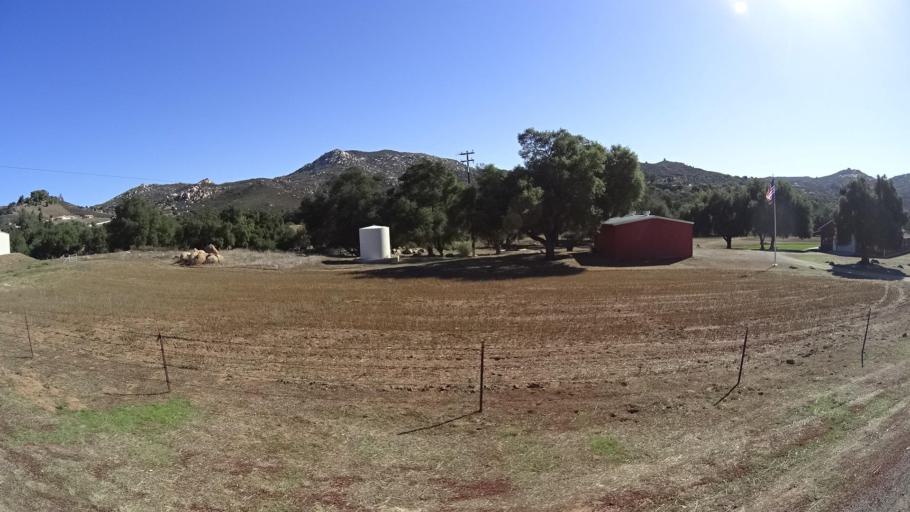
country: US
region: California
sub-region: San Diego County
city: Jamul
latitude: 32.6817
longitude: -116.7538
